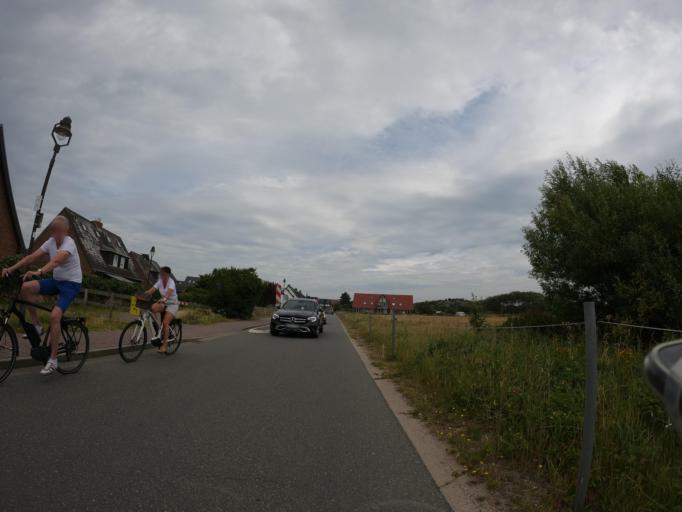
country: DE
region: Schleswig-Holstein
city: Tinnum
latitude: 54.9331
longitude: 8.3273
